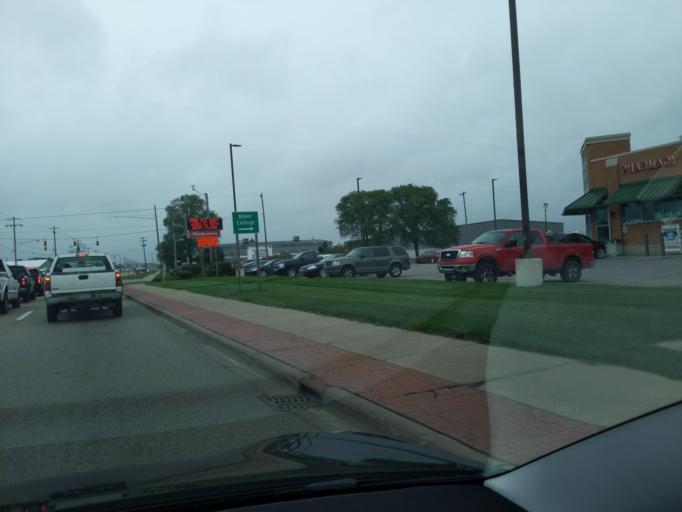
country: US
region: Michigan
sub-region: Wexford County
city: Cadillac
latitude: 44.2662
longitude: -85.4062
